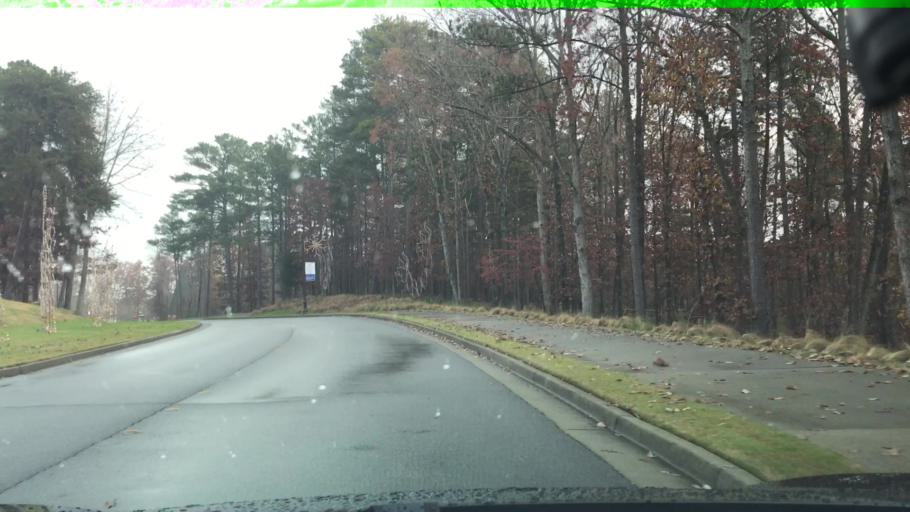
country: US
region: Georgia
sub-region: Gwinnett County
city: Buford
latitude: 34.1768
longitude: -84.0240
